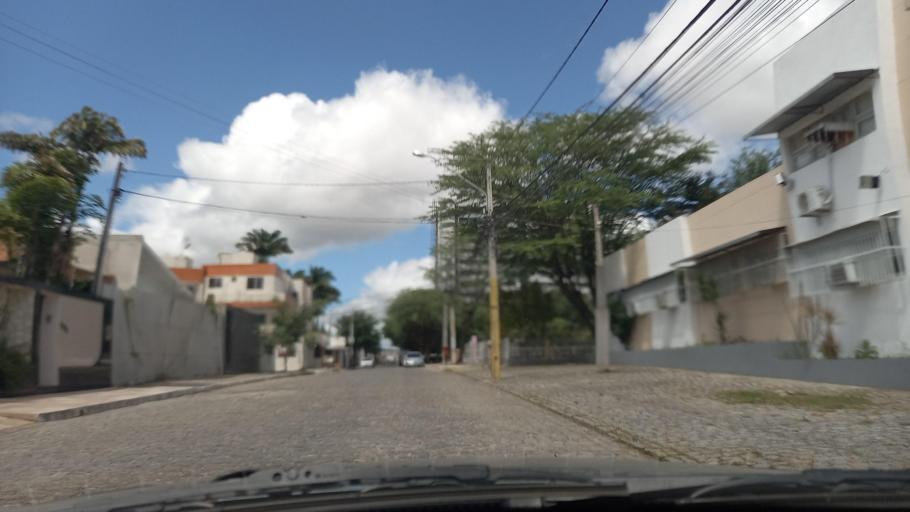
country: BR
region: Pernambuco
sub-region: Caruaru
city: Caruaru
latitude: -8.2670
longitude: -35.9636
